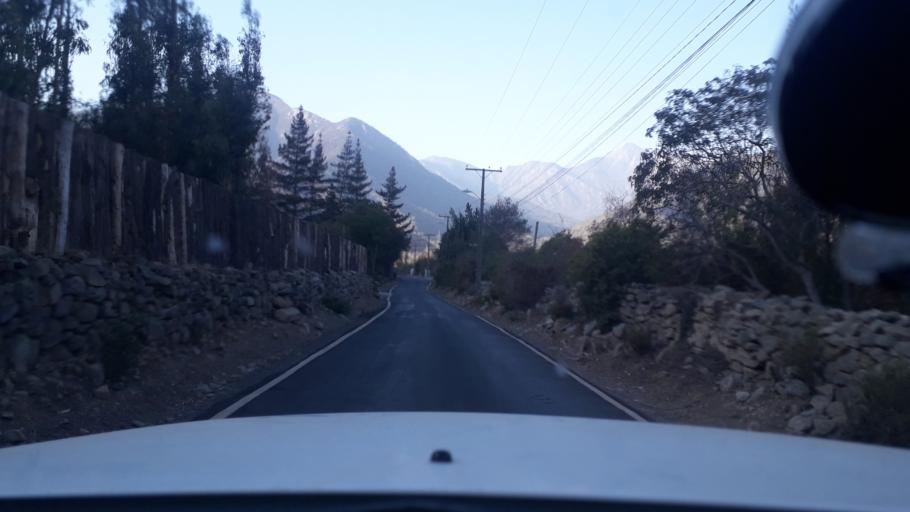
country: CL
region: Valparaiso
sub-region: Provincia de Marga Marga
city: Limache
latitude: -33.0575
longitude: -71.1140
